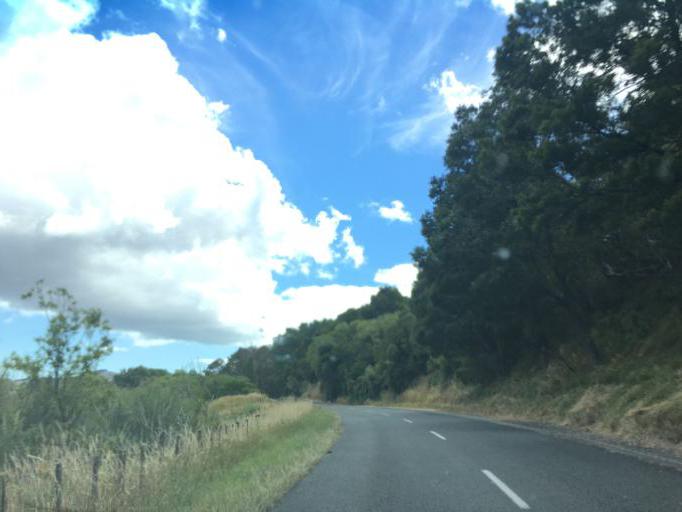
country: NZ
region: Hawke's Bay
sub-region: Hastings District
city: Hastings
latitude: -39.7242
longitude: 176.9227
